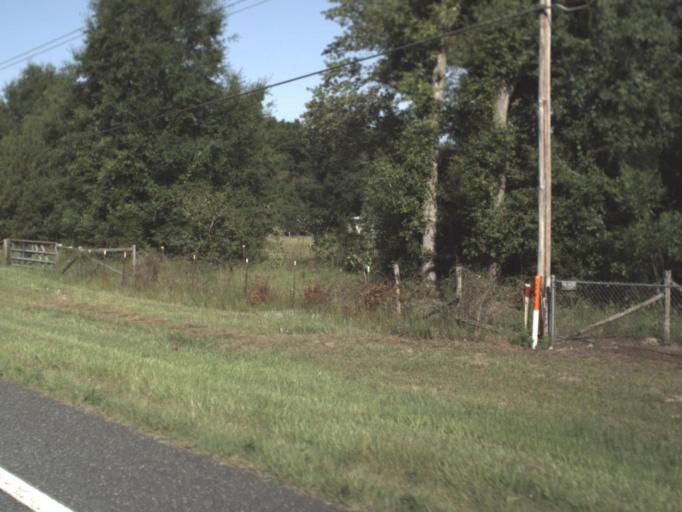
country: US
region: Florida
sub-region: Columbia County
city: Lake City
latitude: 30.0951
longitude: -82.6733
